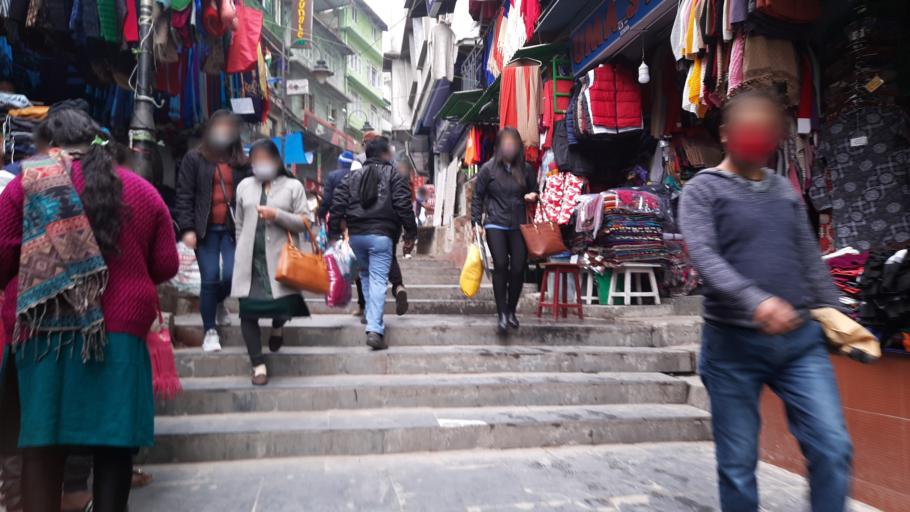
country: IN
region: Sikkim
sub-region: East District
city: Gangtok
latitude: 27.3268
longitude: 88.6118
